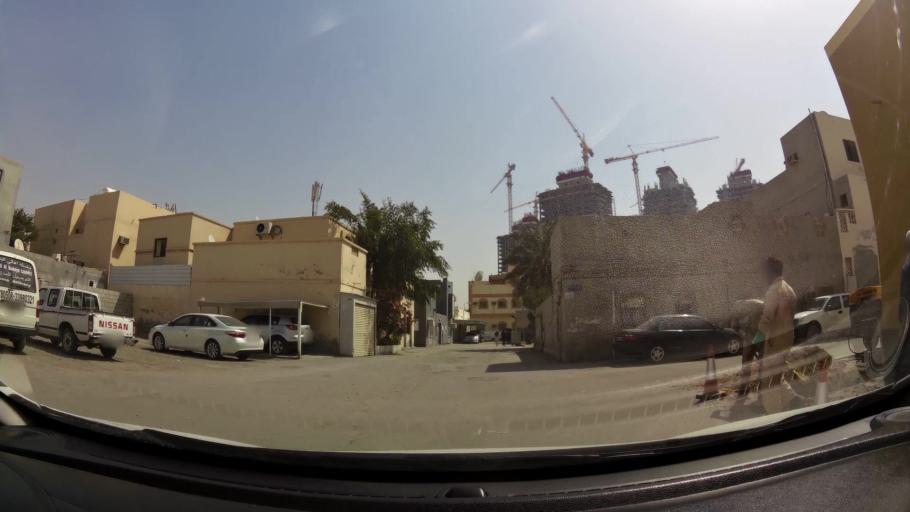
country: BH
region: Manama
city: Jidd Hafs
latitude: 26.2063
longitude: 50.4512
